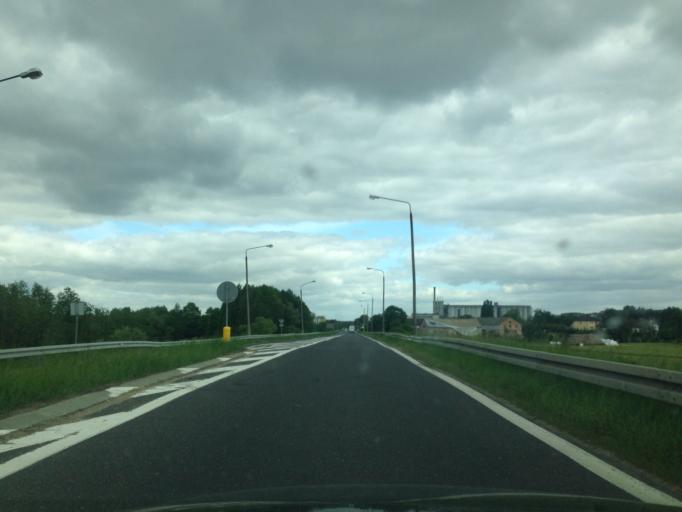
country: PL
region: Kujawsko-Pomorskie
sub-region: Powiat swiecki
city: Swiecie
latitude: 53.3915
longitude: 18.4064
